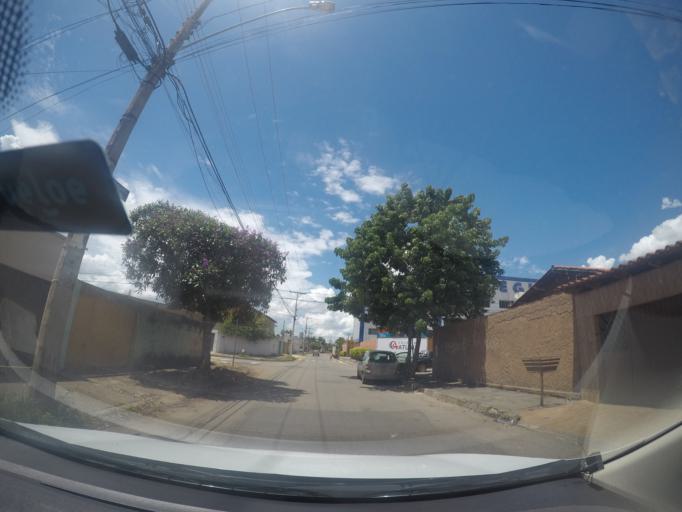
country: BR
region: Goias
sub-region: Goiania
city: Goiania
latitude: -16.7160
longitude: -49.2982
